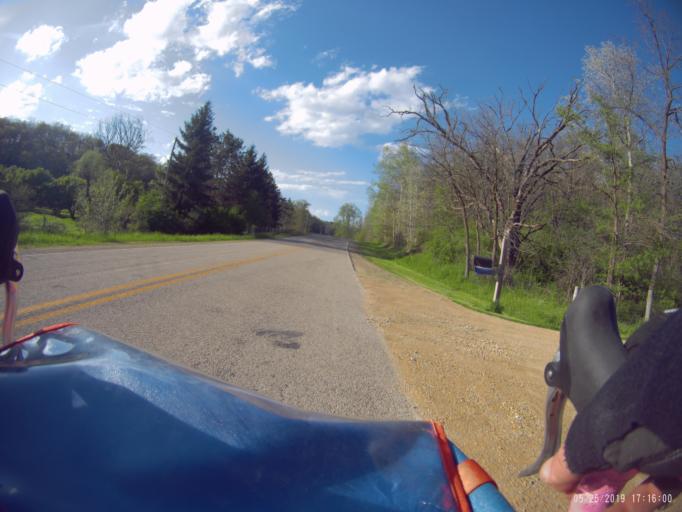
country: US
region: Wisconsin
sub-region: Dane County
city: Mount Horeb
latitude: 42.9681
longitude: -89.7897
